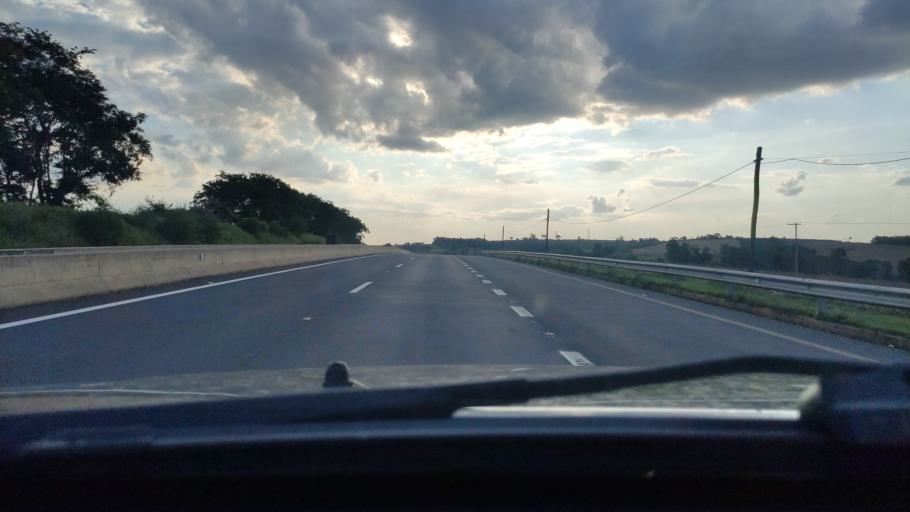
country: BR
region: Sao Paulo
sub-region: Mogi-Mirim
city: Mogi Mirim
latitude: -22.4421
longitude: -47.0445
